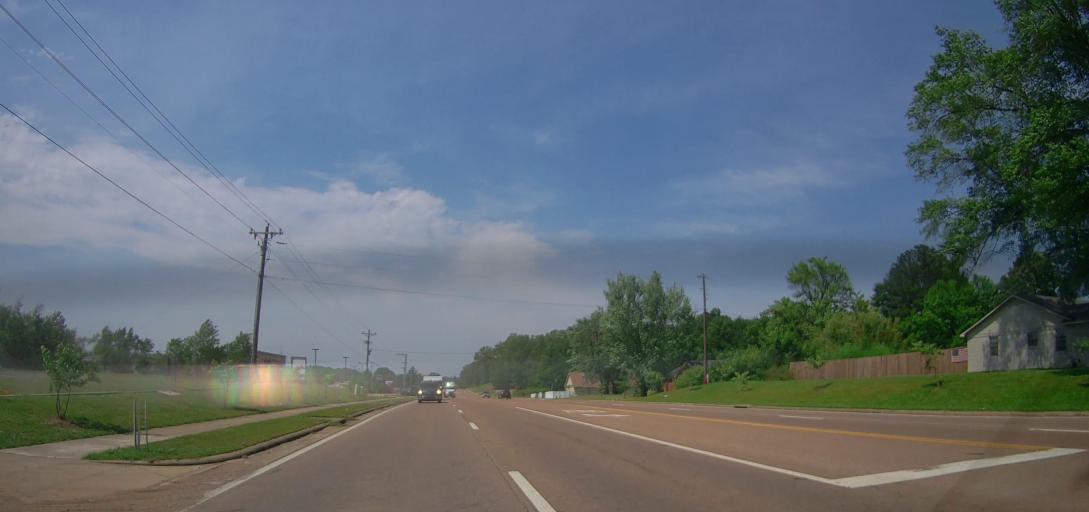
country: US
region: Mississippi
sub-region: De Soto County
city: Olive Branch
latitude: 34.9532
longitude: -89.8305
